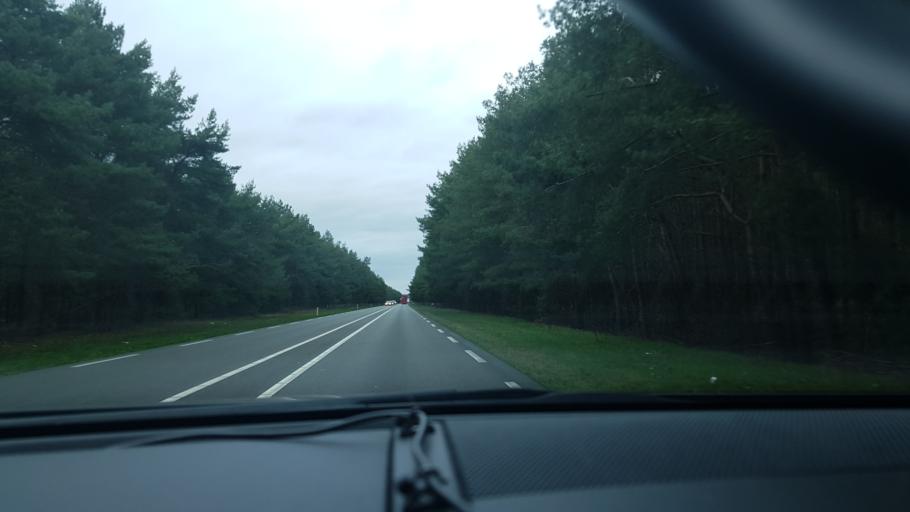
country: NL
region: North Brabant
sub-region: Gemeente Asten
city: Asten
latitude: 51.4453
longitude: 5.7288
